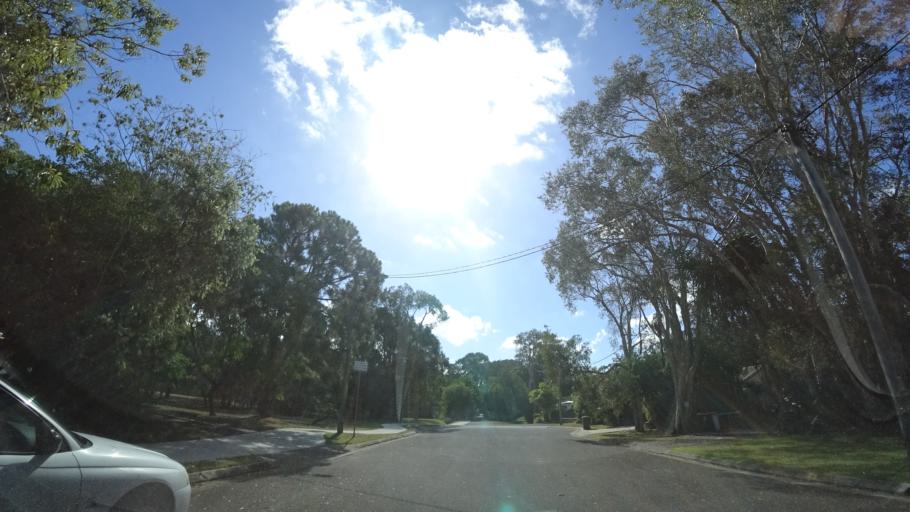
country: AU
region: Queensland
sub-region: Sunshine Coast
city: Mooloolaba
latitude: -26.6185
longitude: 153.0958
